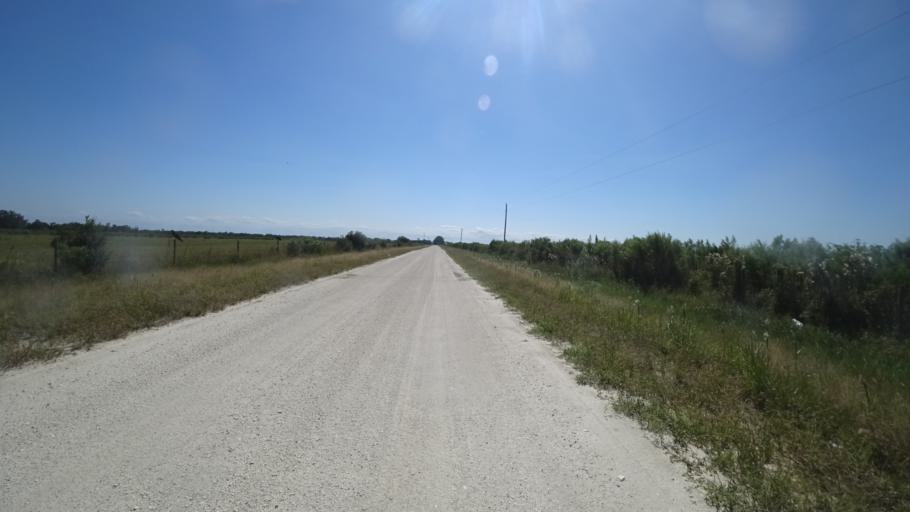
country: US
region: Florida
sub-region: DeSoto County
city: Arcadia
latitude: 27.3349
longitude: -82.0806
